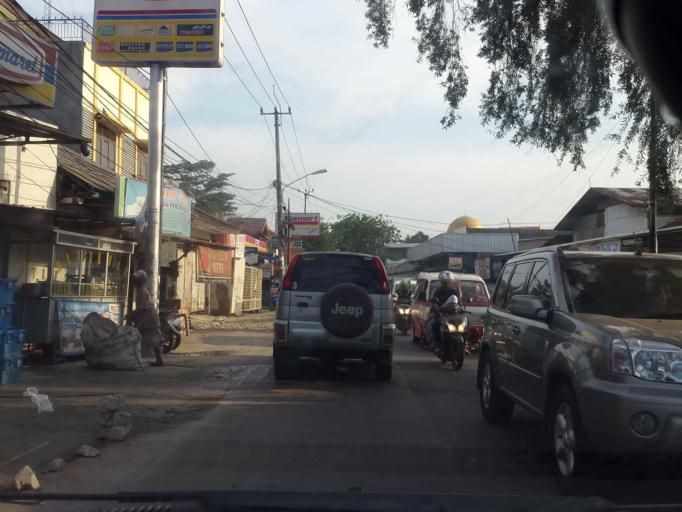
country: ID
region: West Java
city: Ciputat
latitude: -6.2525
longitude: 106.7031
